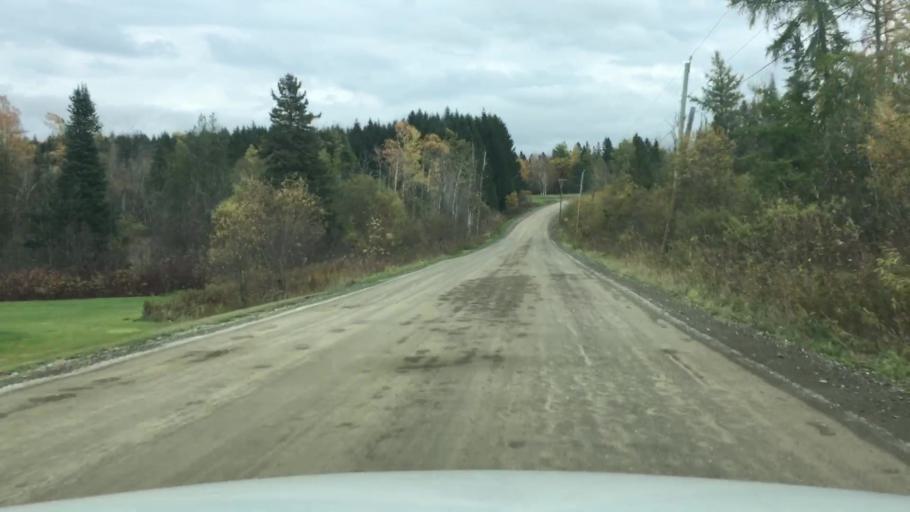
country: US
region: Maine
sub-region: Aroostook County
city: Easton
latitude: 46.5222
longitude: -67.8911
